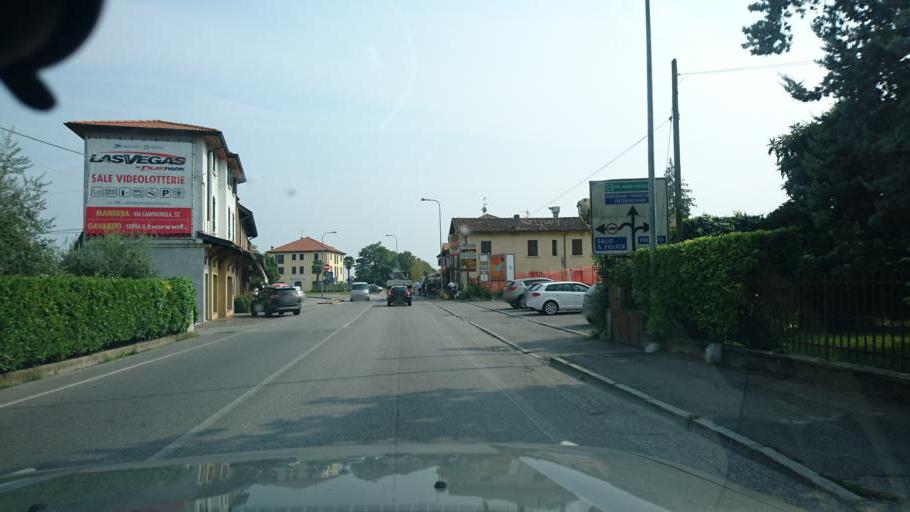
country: IT
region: Lombardy
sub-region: Provincia di Brescia
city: Cunettone-Villa
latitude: 45.5876
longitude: 10.5163
